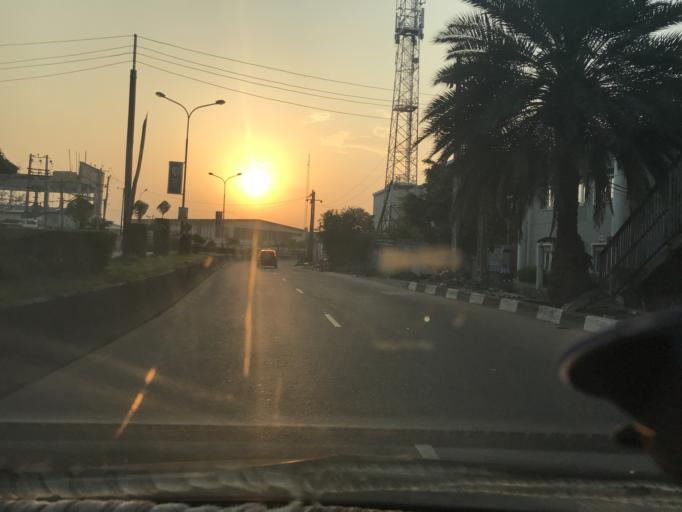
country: NG
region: Lagos
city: Makoko
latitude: 6.4974
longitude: 3.3792
